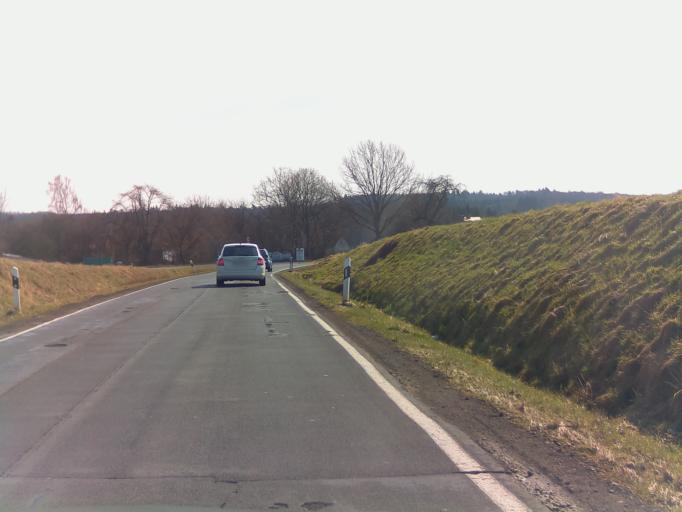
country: DE
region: Hesse
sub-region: Regierungsbezirk Giessen
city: Grunberg
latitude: 50.6253
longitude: 9.0227
